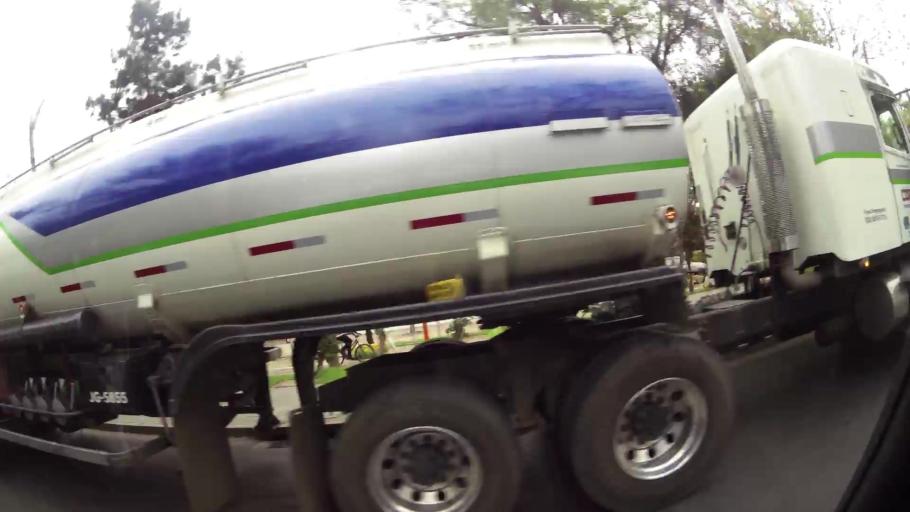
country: CL
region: Santiago Metropolitan
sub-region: Provincia de Santiago
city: Lo Prado
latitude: -33.5199
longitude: -70.7556
